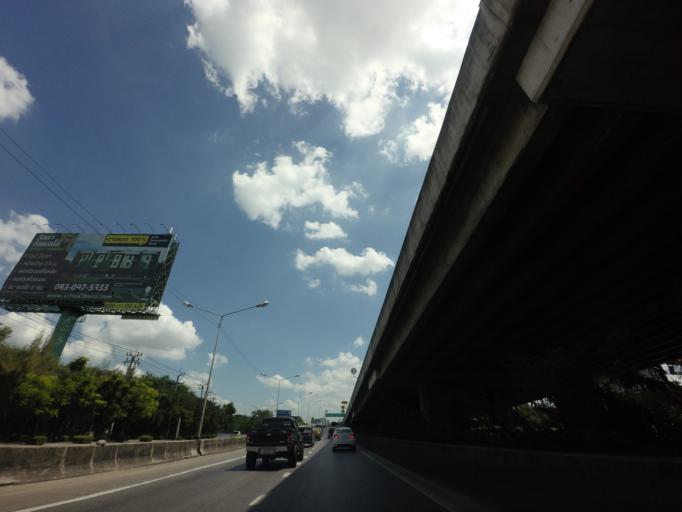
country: TH
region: Bangkok
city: Suan Luang
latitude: 13.7422
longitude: 100.6389
